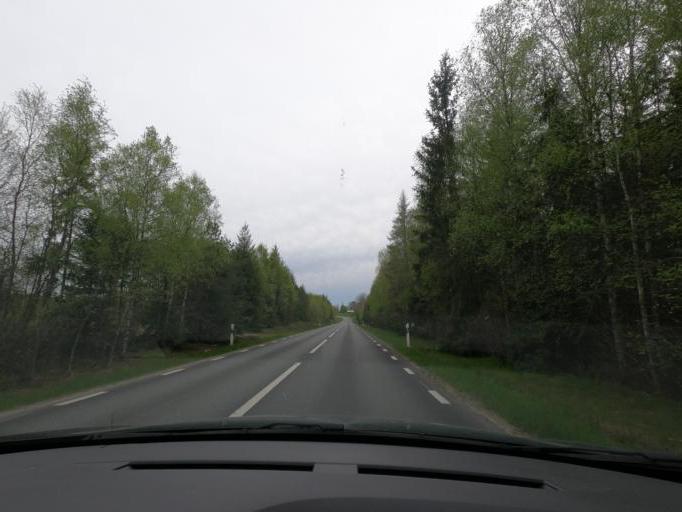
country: SE
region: Joenkoeping
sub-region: Varnamo Kommun
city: Bredaryd
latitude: 57.1943
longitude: 13.7612
